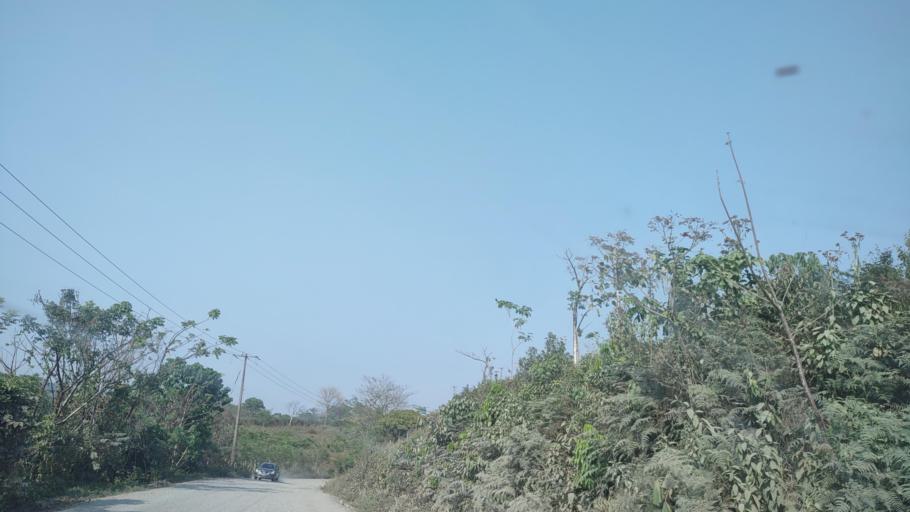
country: MX
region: Tabasco
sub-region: Huimanguillo
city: Francisco Rueda
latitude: 17.6433
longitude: -93.9107
